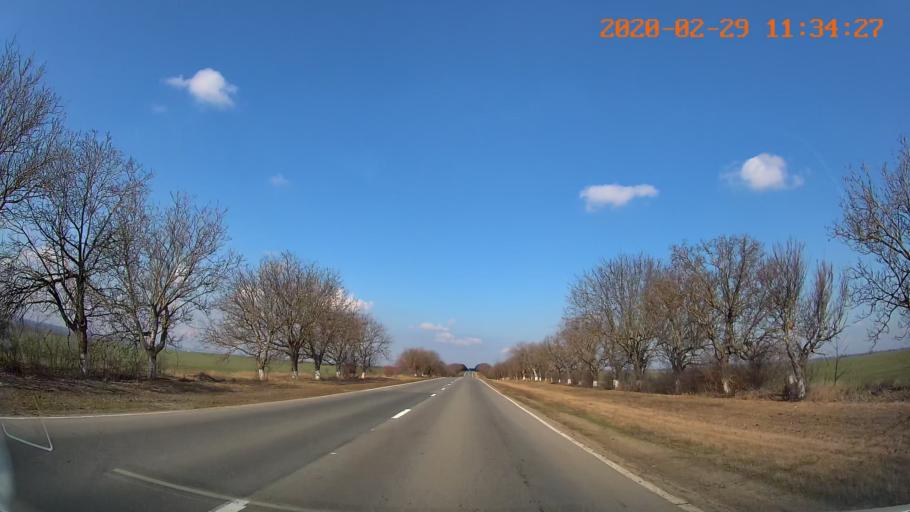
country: MD
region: Rezina
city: Saharna
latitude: 47.5660
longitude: 29.0736
